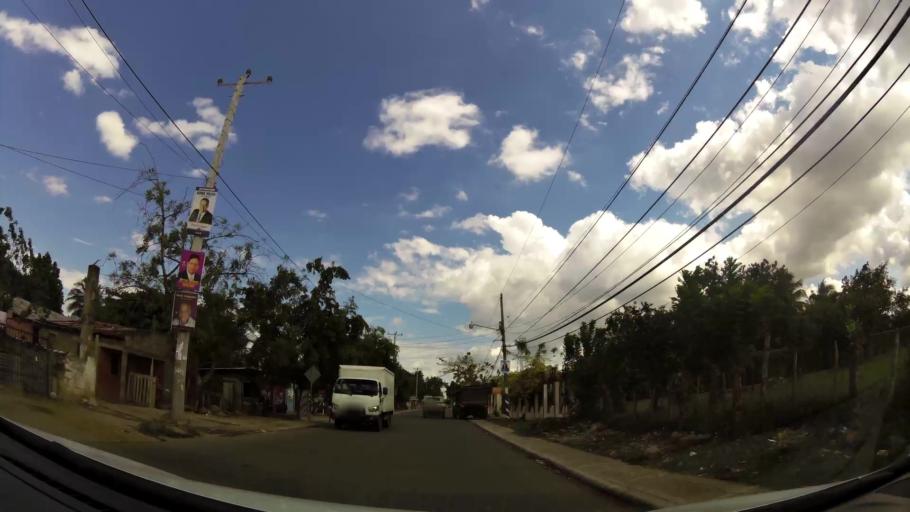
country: DO
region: Santiago
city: Licey al Medio
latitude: 19.3890
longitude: -70.6362
